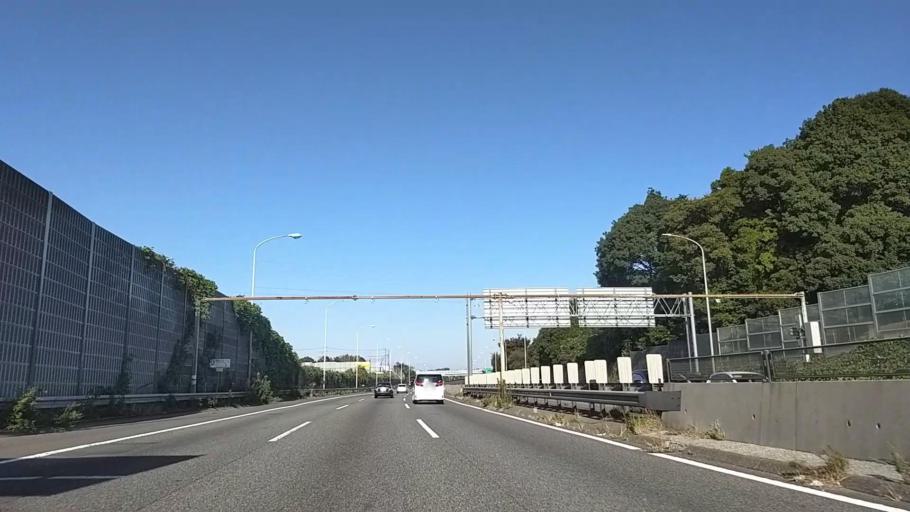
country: JP
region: Kanagawa
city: Yokohama
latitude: 35.4575
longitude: 139.5475
